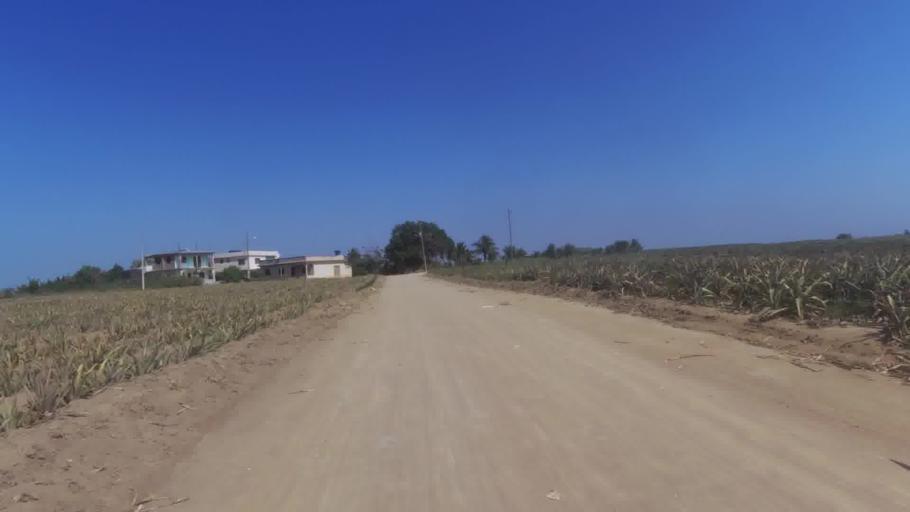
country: BR
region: Espirito Santo
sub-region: Marataizes
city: Marataizes
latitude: -21.1058
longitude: -40.8617
